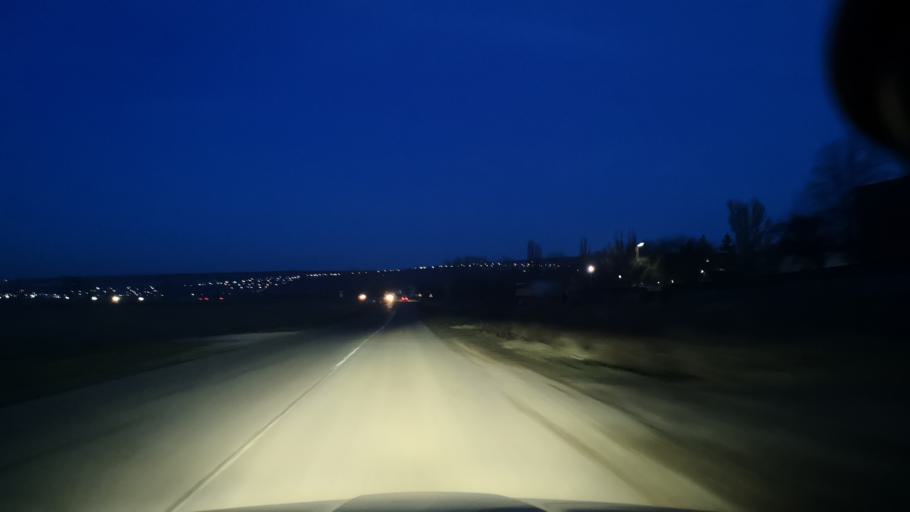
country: MD
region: Orhei
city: Orhei
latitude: 47.3429
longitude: 28.7717
